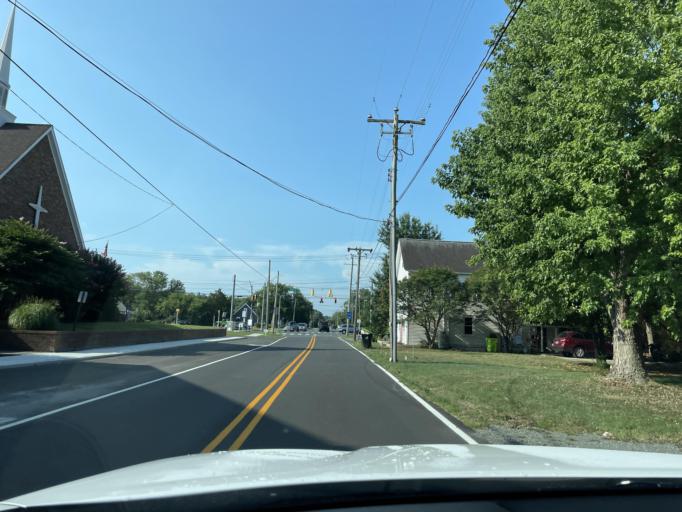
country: US
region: Delaware
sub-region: Sussex County
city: Ocean View
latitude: 38.5448
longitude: -75.0890
